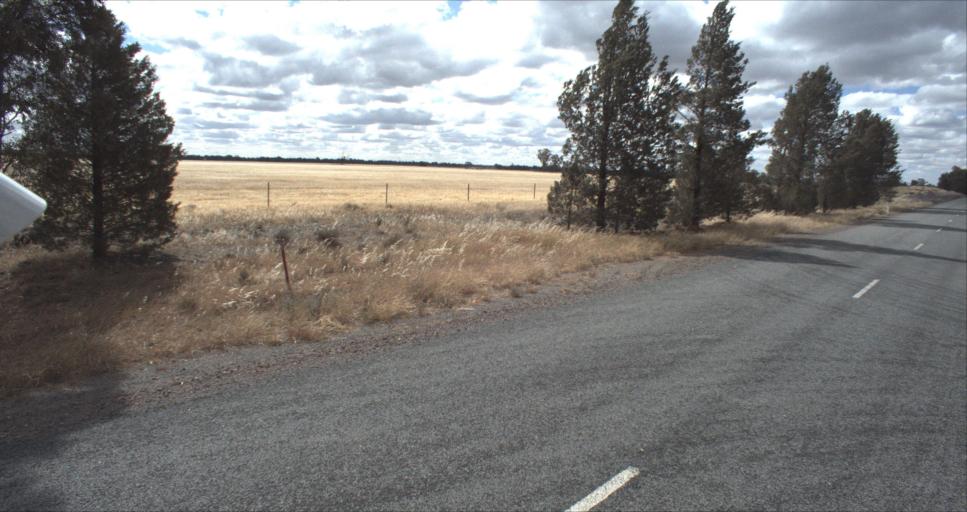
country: AU
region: New South Wales
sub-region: Leeton
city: Leeton
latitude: -34.6758
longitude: 146.3466
